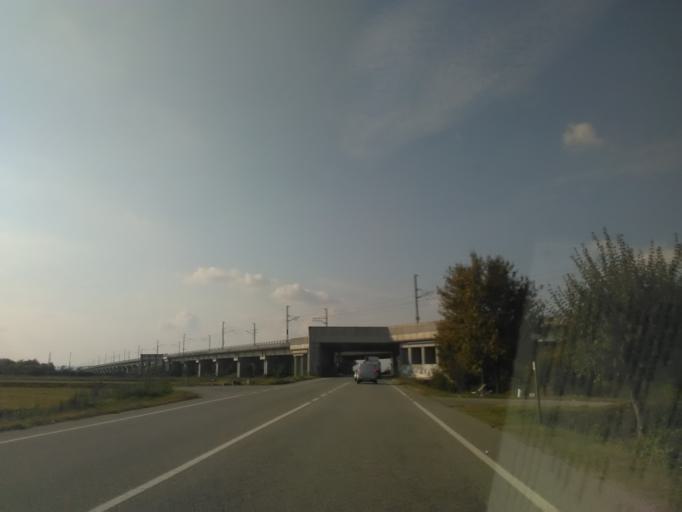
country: IT
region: Piedmont
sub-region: Provincia di Vercelli
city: Balocco
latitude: 45.4392
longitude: 8.2451
